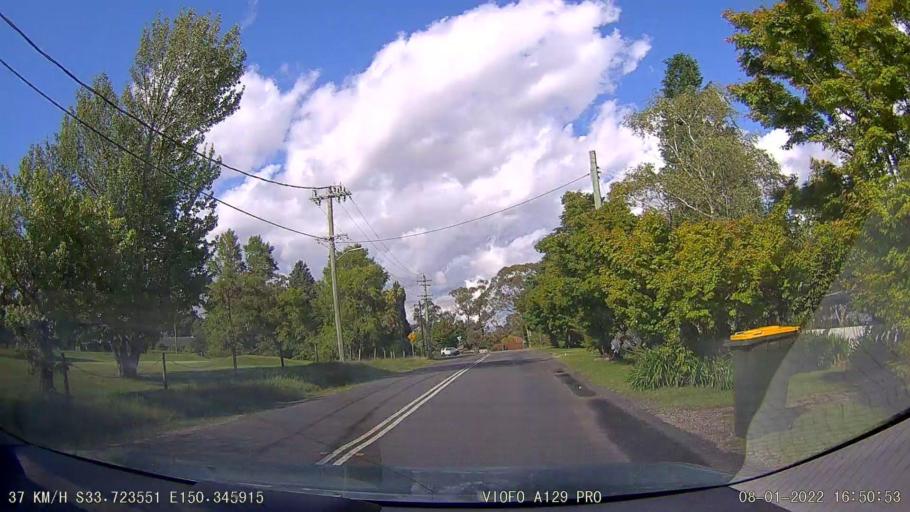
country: AU
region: New South Wales
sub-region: Blue Mountains Municipality
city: Leura
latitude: -33.7236
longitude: 150.3460
